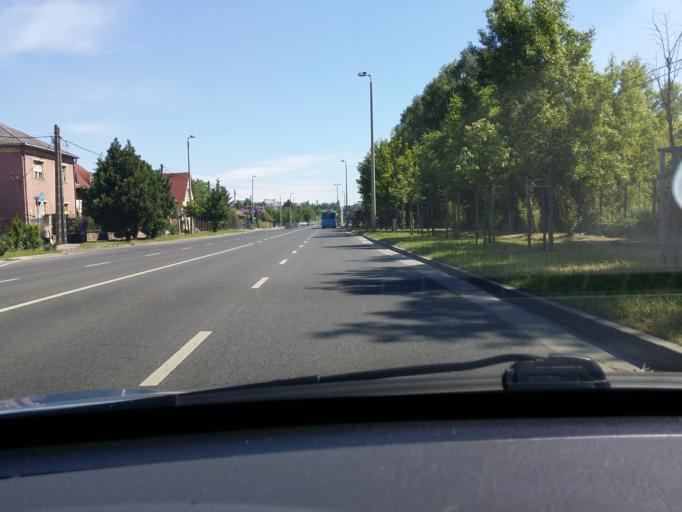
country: HU
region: Budapest
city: Budapest IV. keruelet
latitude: 47.5845
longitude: 19.0931
